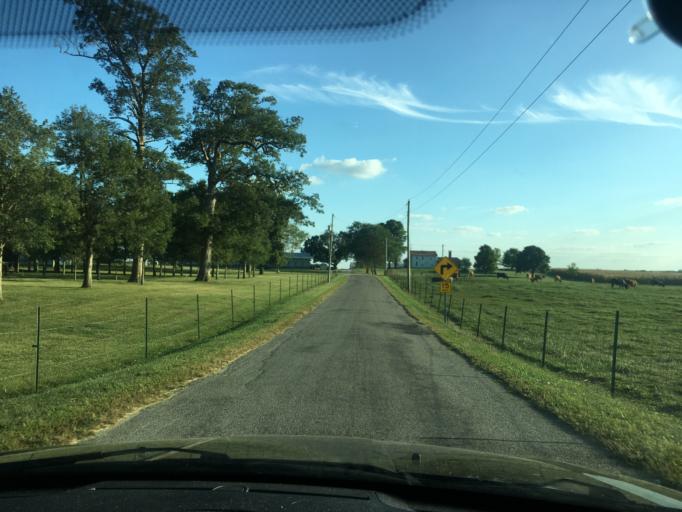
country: US
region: Ohio
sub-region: Logan County
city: West Liberty
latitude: 40.2198
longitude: -83.7345
